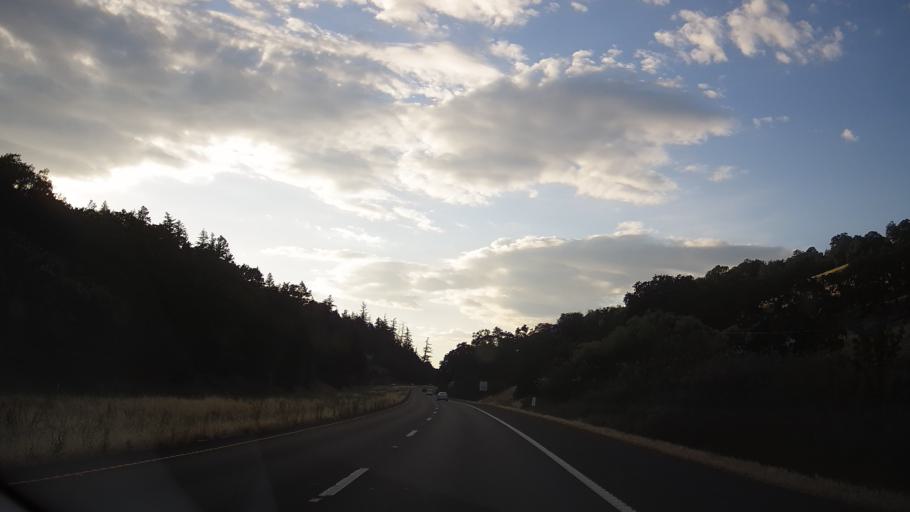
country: US
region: California
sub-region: Mendocino County
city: Talmage
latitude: 39.0631
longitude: -123.1631
